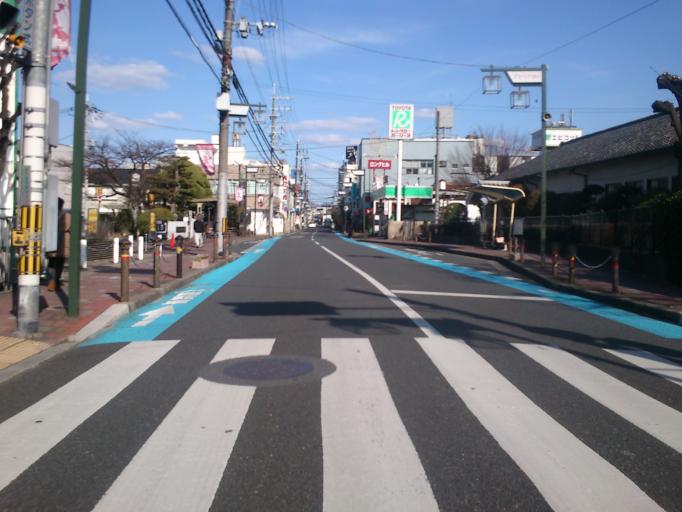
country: JP
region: Kyoto
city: Muko
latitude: 34.9262
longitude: 135.6952
